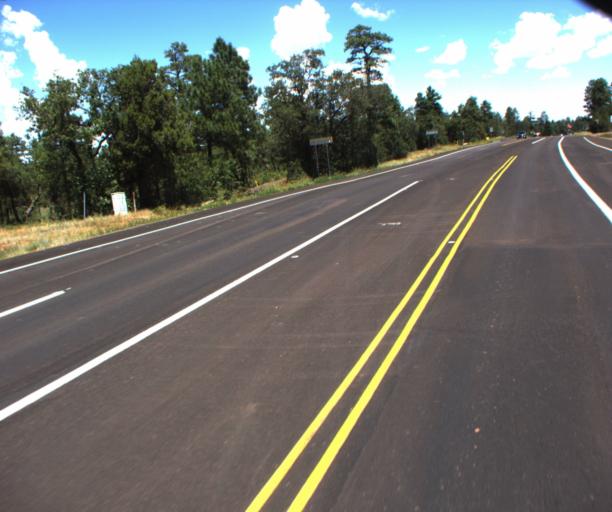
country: US
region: Arizona
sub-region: Navajo County
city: Show Low
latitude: 34.2361
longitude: -110.0639
